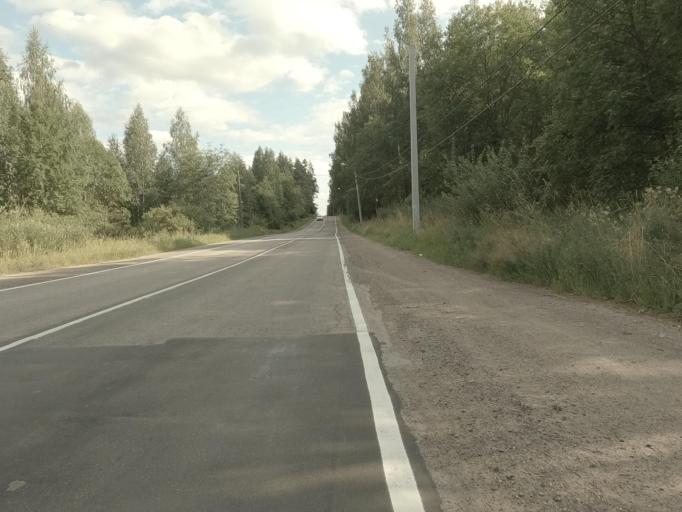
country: RU
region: Leningrad
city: Kamennogorsk
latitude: 60.9386
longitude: 29.1562
